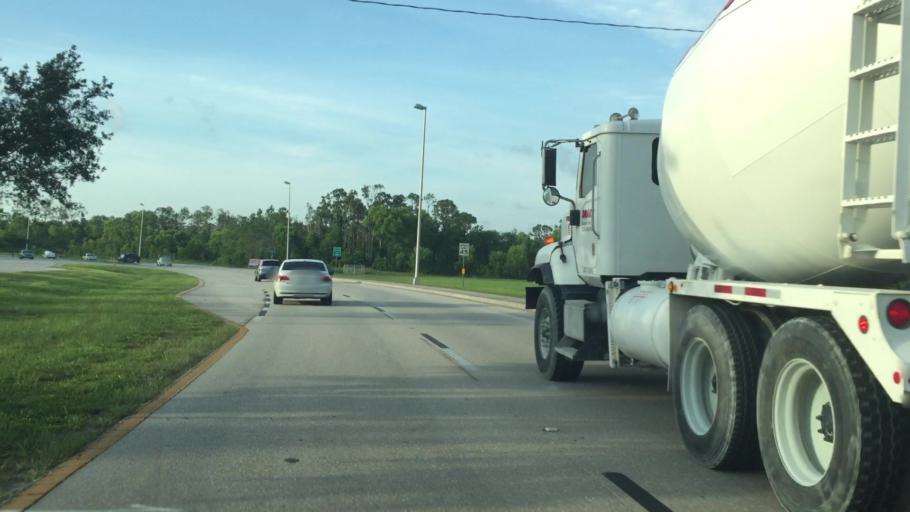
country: US
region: Florida
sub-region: Lee County
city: Three Oaks
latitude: 26.4691
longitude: -81.7935
